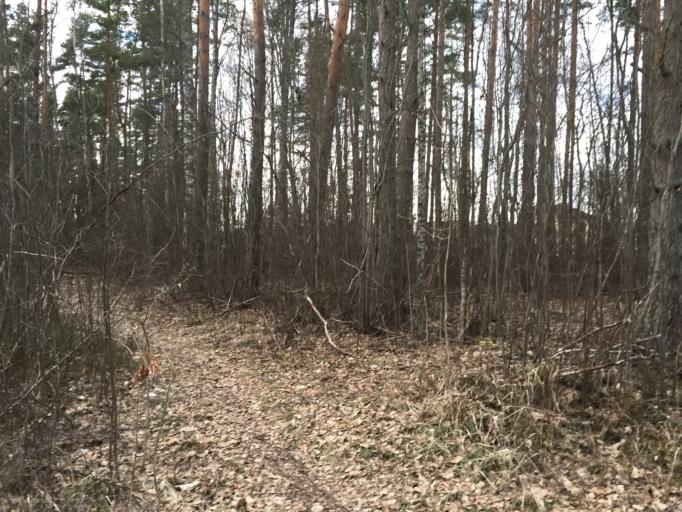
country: LV
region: Babite
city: Pinki
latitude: 56.9177
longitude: 23.8679
